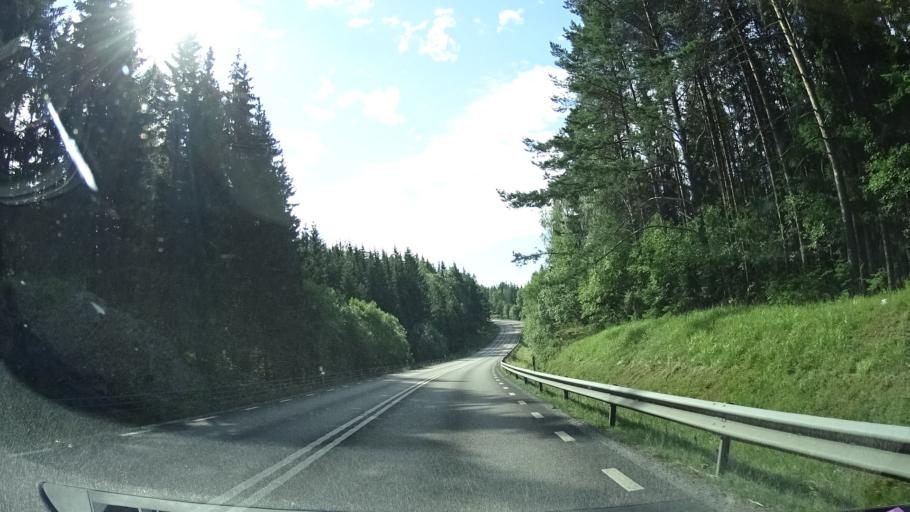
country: SE
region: Vaermland
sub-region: Arjangs Kommun
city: Toecksfors
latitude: 59.5012
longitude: 11.8767
